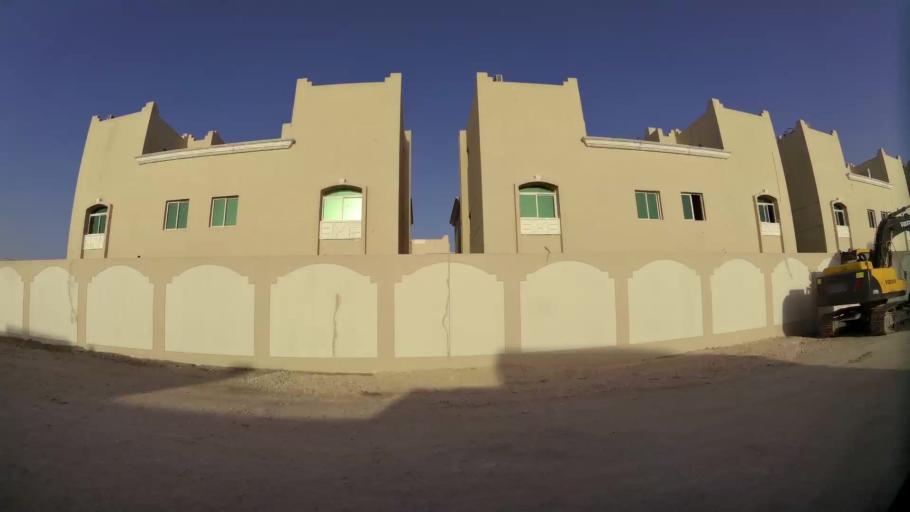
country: QA
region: Baladiyat ar Rayyan
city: Ar Rayyan
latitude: 25.3238
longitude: 51.4527
